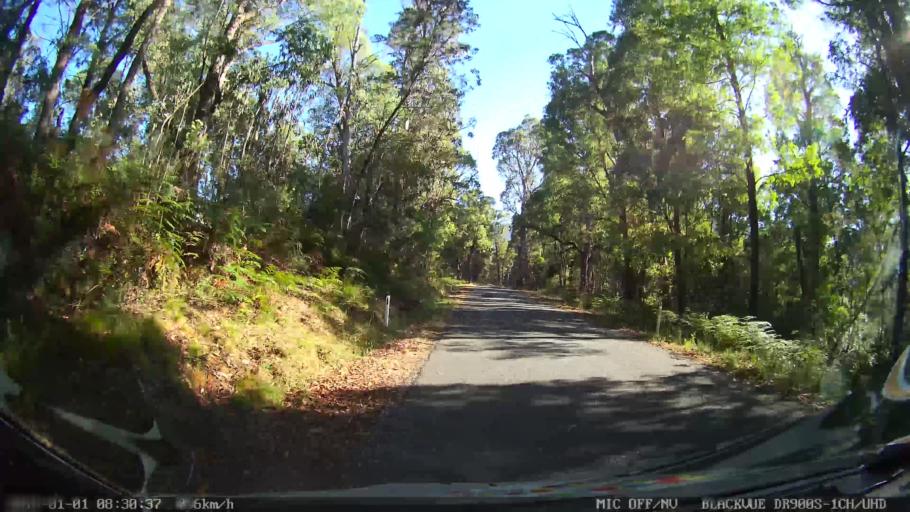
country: AU
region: New South Wales
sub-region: Snowy River
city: Jindabyne
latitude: -36.3749
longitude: 148.1994
